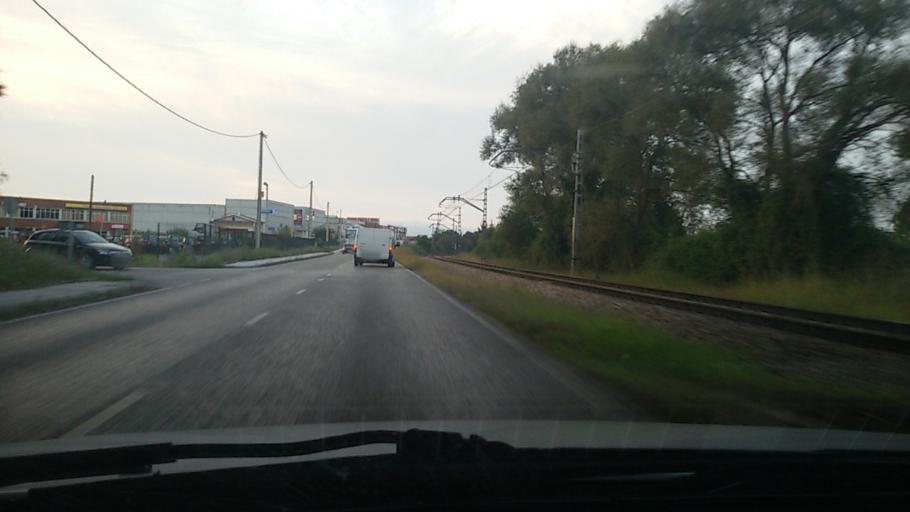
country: ES
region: Asturias
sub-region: Province of Asturias
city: Lugones
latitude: 43.3926
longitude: -5.7881
